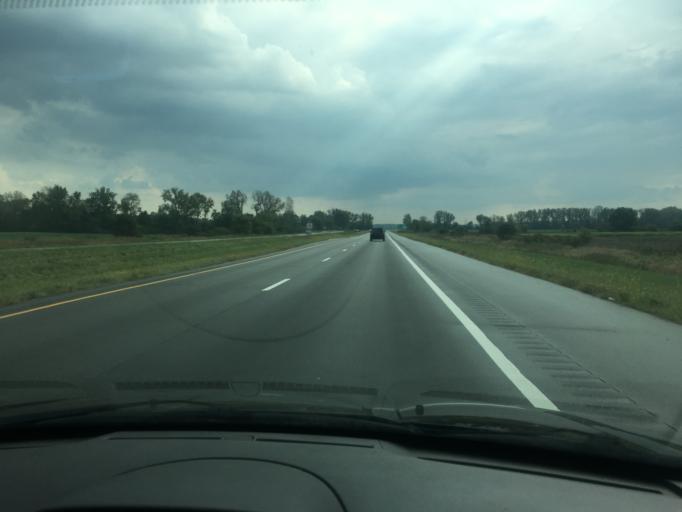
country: US
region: Ohio
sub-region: Clark County
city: Northridge
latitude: 40.0009
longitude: -83.8107
